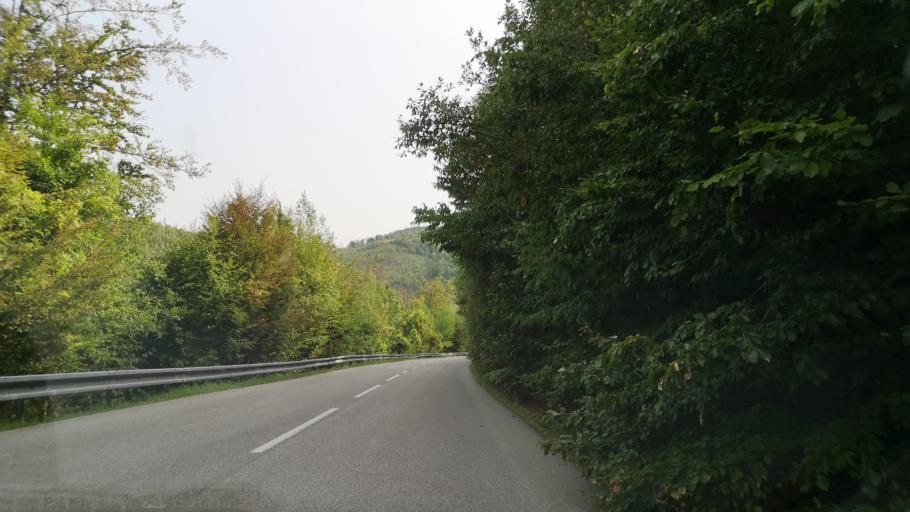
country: SK
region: Banskobystricky
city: Tisovec
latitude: 48.5822
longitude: 20.0026
